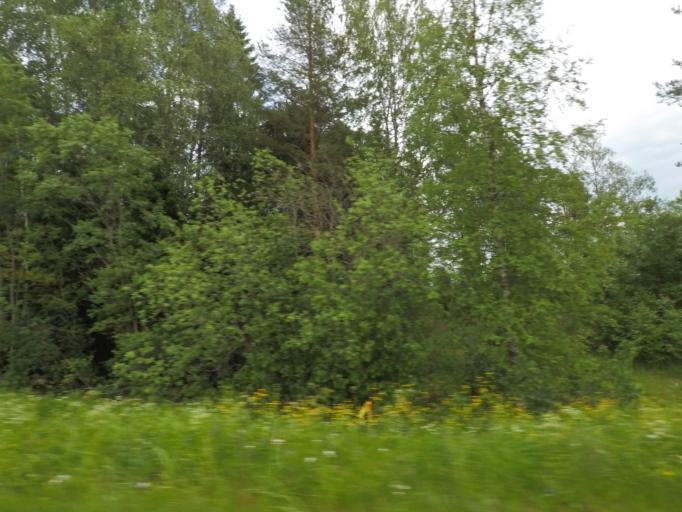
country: FI
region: Uusimaa
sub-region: Porvoo
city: Pukkila
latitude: 60.8024
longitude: 25.4754
